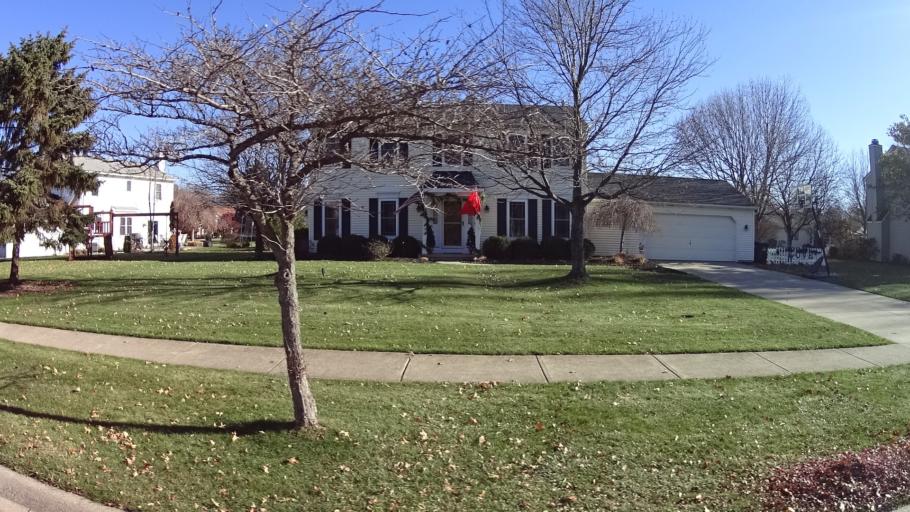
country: US
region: Ohio
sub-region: Lorain County
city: Avon Center
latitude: 41.4881
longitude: -81.9911
